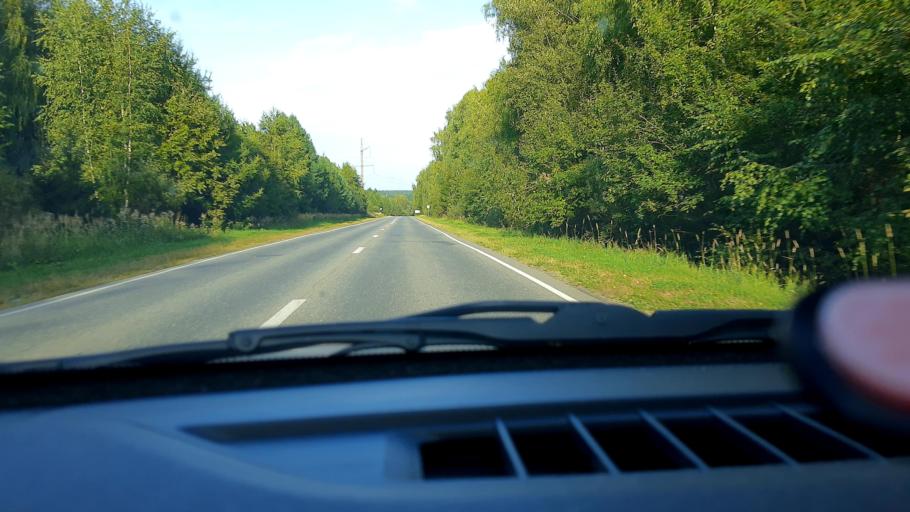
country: RU
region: Nizjnij Novgorod
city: Gorodets
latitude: 56.6626
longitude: 43.5506
